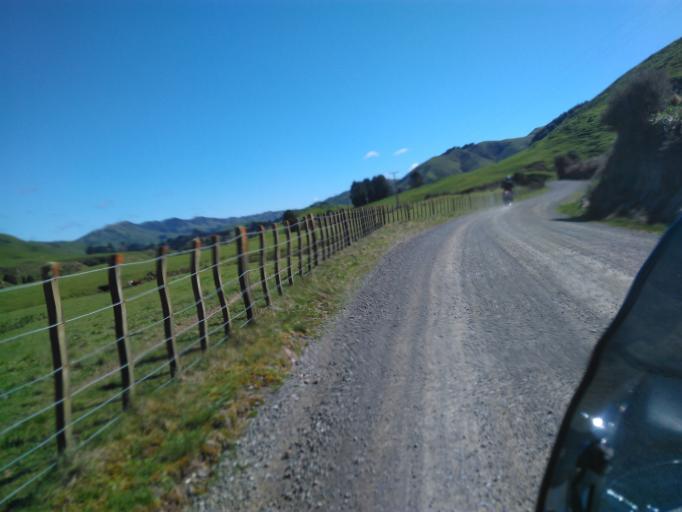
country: NZ
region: Bay of Plenty
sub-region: Opotiki District
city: Opotiki
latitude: -38.3079
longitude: 177.5627
